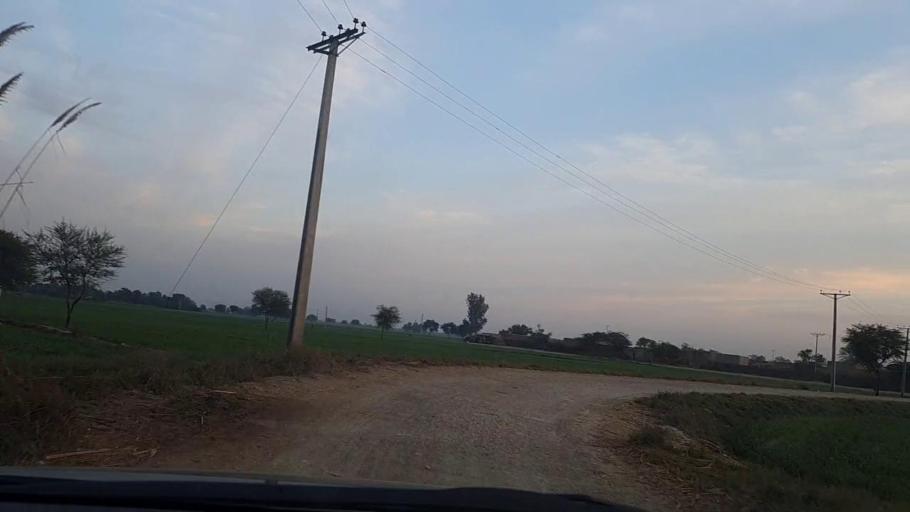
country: PK
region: Sindh
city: Sakrand
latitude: 26.2025
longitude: 68.3181
